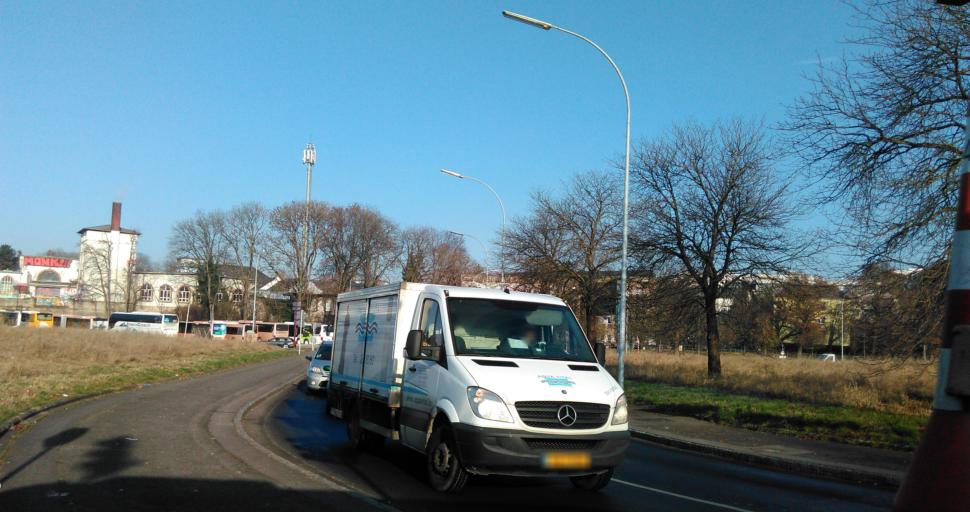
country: LU
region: Luxembourg
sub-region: Canton de Luxembourg
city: Luxembourg
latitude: 49.5990
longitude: 6.1170
